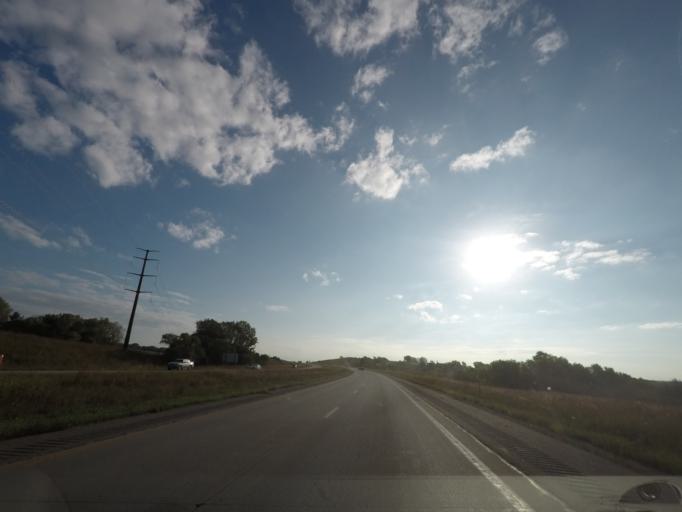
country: US
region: Iowa
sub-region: Warren County
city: Norwalk
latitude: 41.4980
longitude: -93.6088
